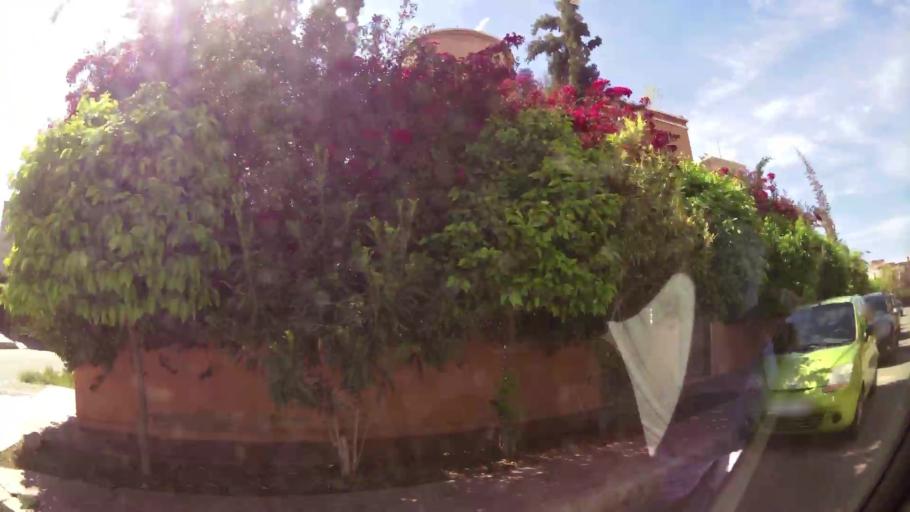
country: MA
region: Marrakech-Tensift-Al Haouz
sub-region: Marrakech
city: Marrakesh
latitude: 31.6780
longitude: -8.0045
